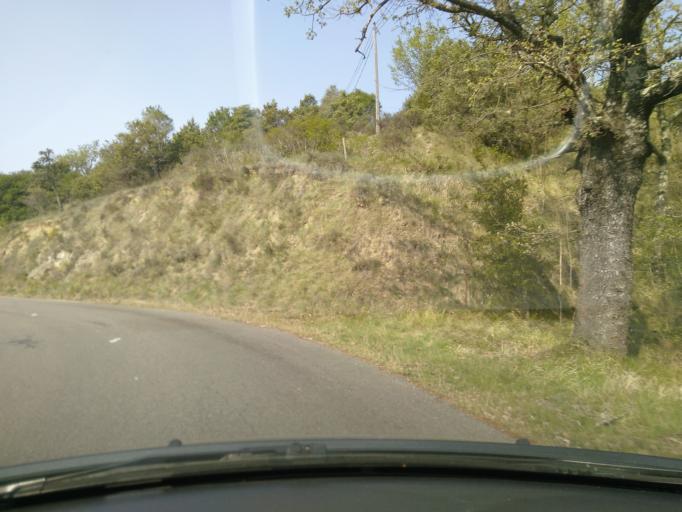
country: FR
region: Rhone-Alpes
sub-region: Departement de l'Ardeche
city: Ruoms
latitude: 44.4526
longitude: 4.3878
